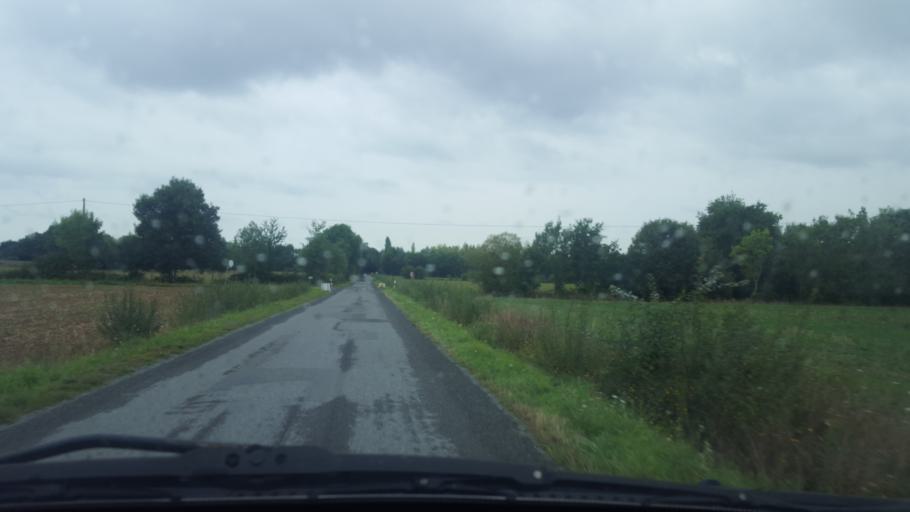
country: FR
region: Pays de la Loire
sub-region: Departement de la Loire-Atlantique
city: Saint-Lumine-de-Coutais
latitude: 47.0488
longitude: -1.6912
